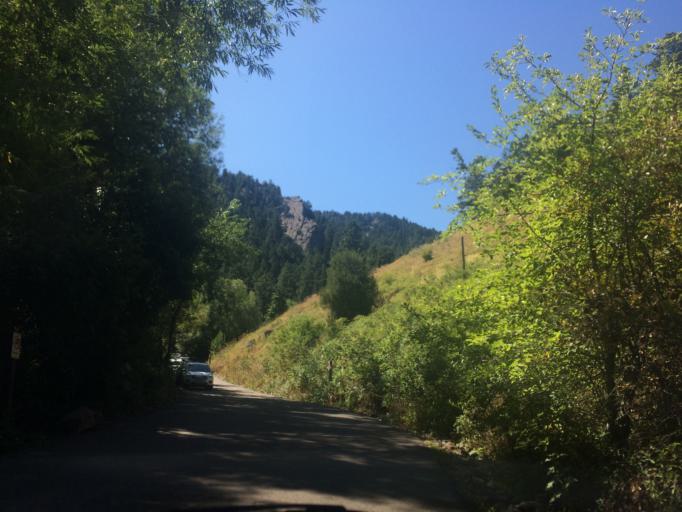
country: US
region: Colorado
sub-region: Boulder County
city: Boulder
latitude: 39.9983
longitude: -105.2921
